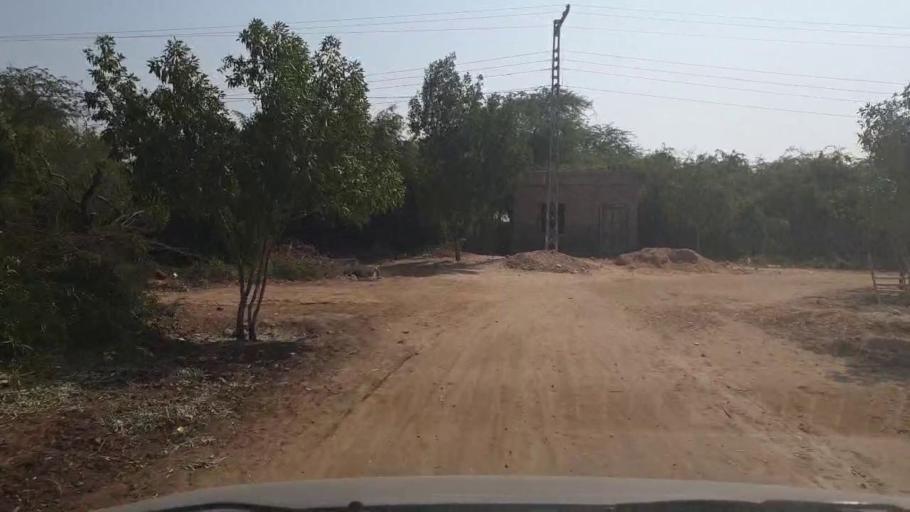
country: PK
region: Sindh
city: Mirwah Gorchani
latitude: 25.2748
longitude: 69.1361
